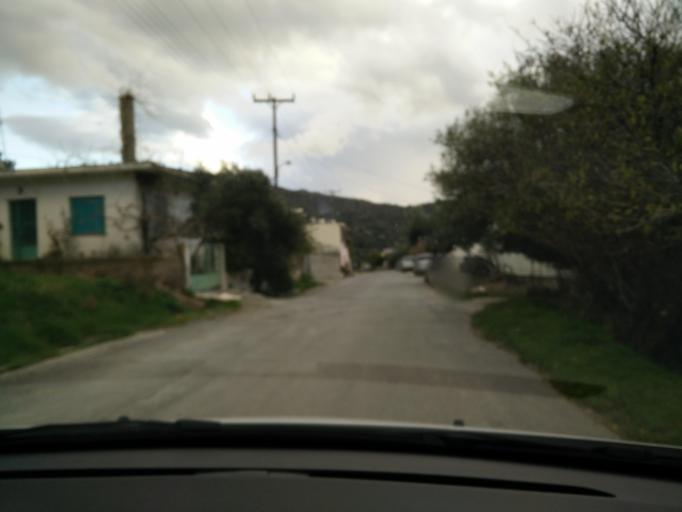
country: GR
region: Crete
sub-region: Nomos Lasithiou
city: Kritsa
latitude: 35.0941
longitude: 25.6868
